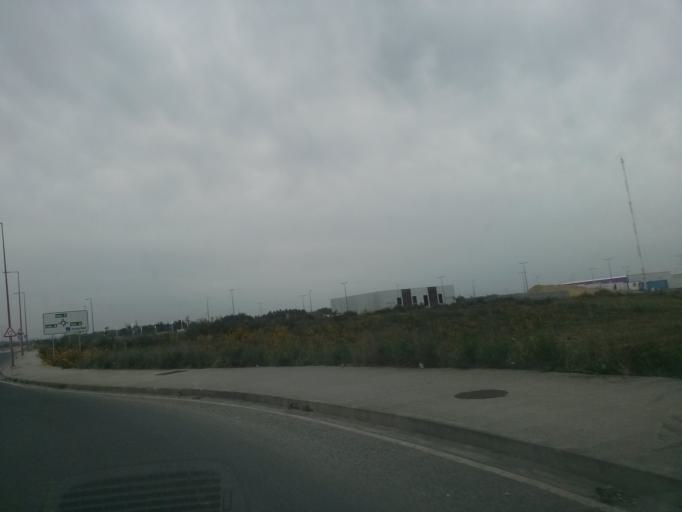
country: ES
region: Galicia
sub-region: Provincia de Lugo
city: Lugo
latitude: 43.0426
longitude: -7.5556
